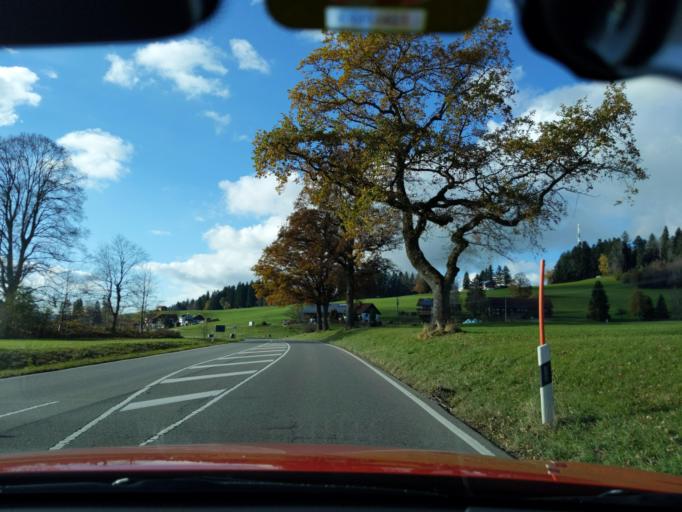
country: DE
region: Bavaria
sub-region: Swabia
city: Oberreute
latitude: 47.5688
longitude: 9.9417
